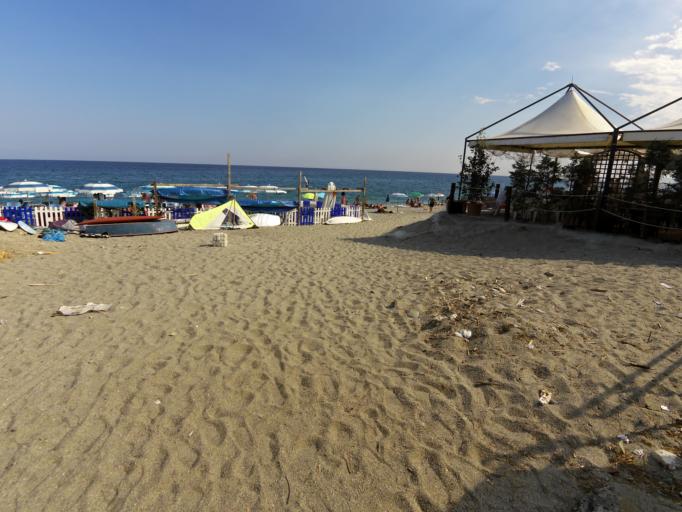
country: IT
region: Calabria
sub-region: Provincia di Reggio Calabria
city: Siderno
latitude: 38.2659
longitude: 16.2973
